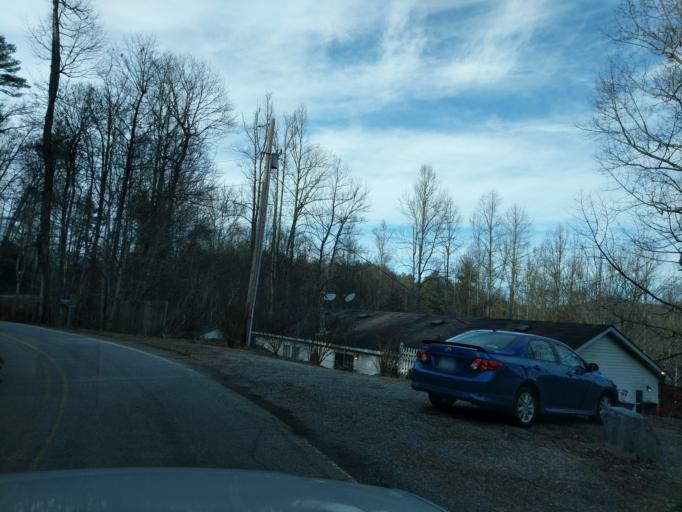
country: US
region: North Carolina
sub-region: Haywood County
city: Cove Creek
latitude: 35.6568
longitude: -83.0053
